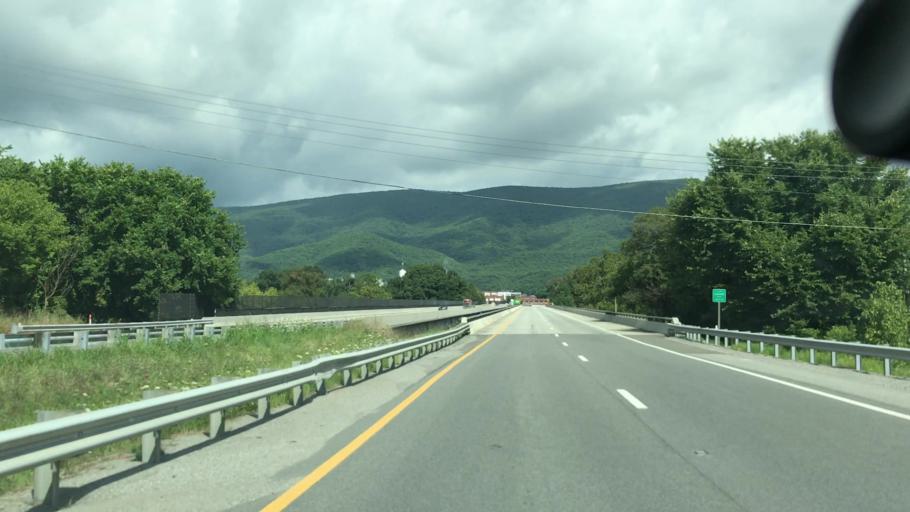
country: US
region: Virginia
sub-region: Giles County
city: Pearisburg
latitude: 37.3379
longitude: -80.7555
